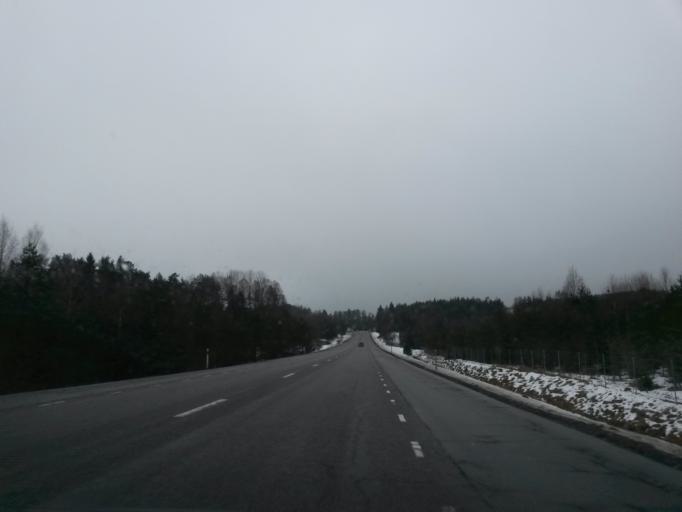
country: SE
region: Vaestra Goetaland
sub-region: Boras Kommun
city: Viskafors
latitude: 57.5998
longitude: 12.8718
